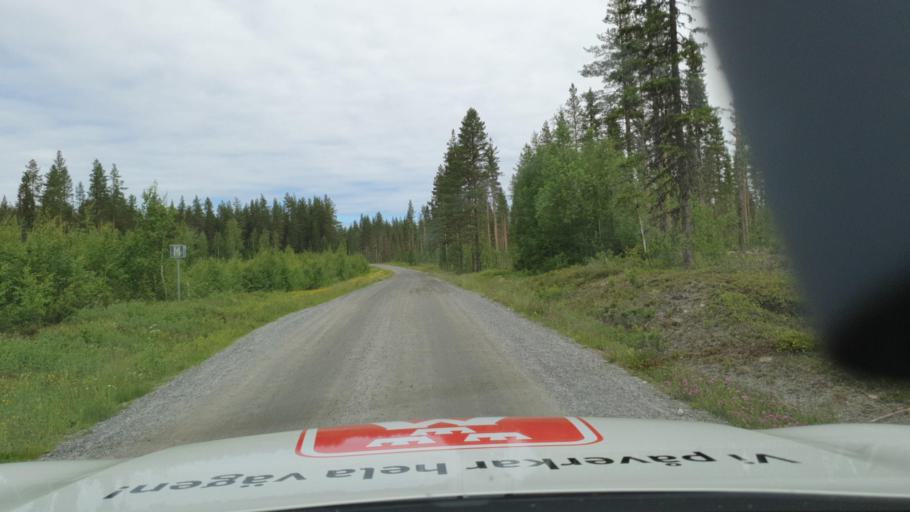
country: SE
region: Vaesterbotten
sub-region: Skelleftea Kommun
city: Forsbacka
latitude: 64.5201
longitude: 20.3253
